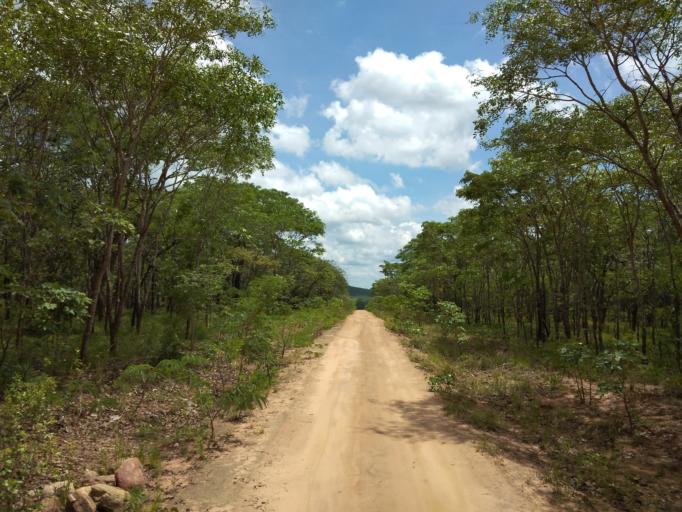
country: ZM
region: Central
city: Mkushi
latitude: -14.0109
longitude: 29.9580
